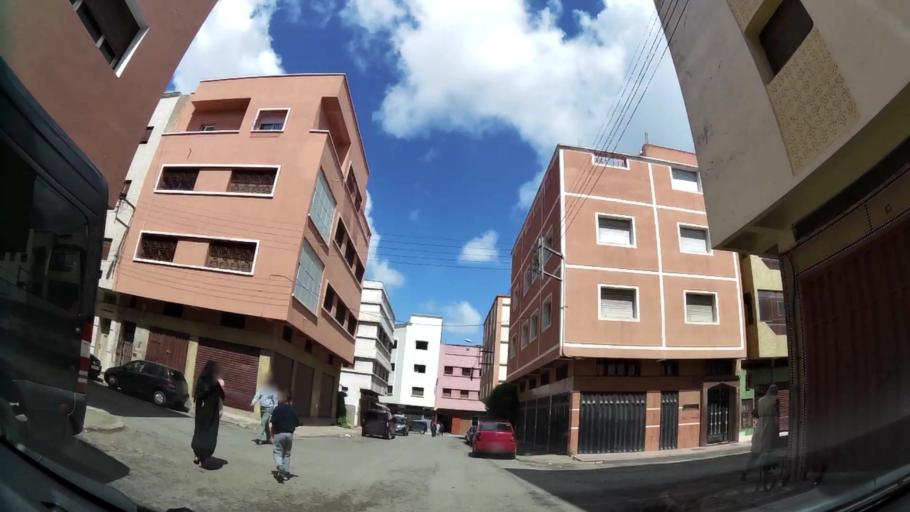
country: MA
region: Grand Casablanca
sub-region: Casablanca
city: Casablanca
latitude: 33.5340
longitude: -7.5837
